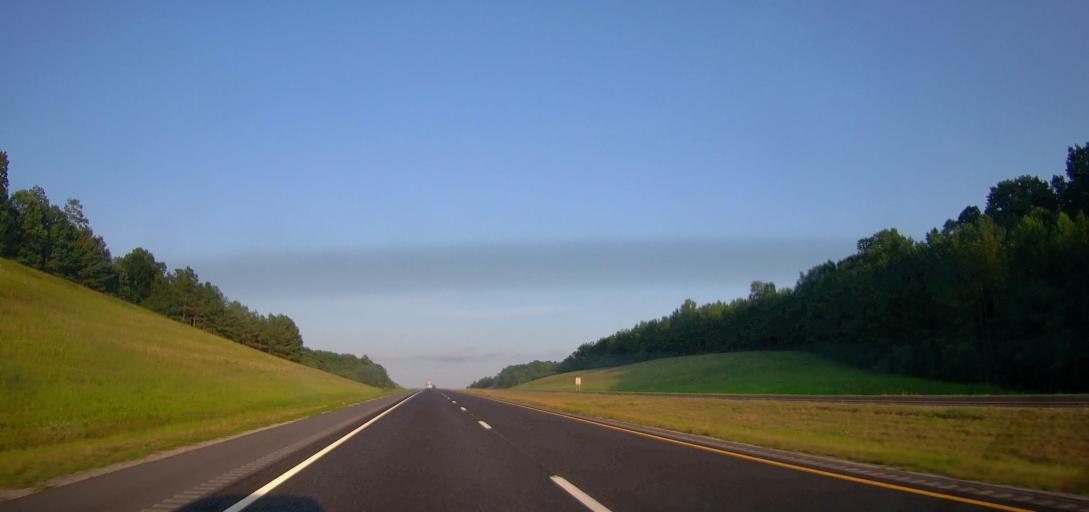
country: US
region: Alabama
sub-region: Marion County
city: Guin
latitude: 34.0354
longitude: -87.8758
